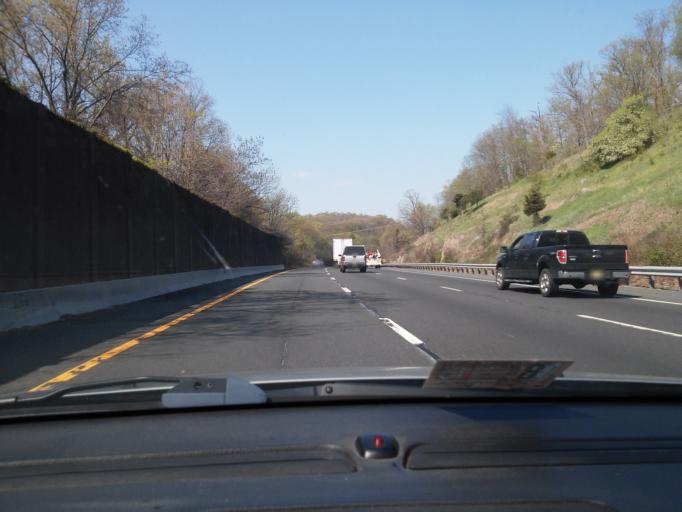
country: US
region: New Jersey
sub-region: Union County
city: Berkeley Heights
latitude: 40.6634
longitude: -74.4213
